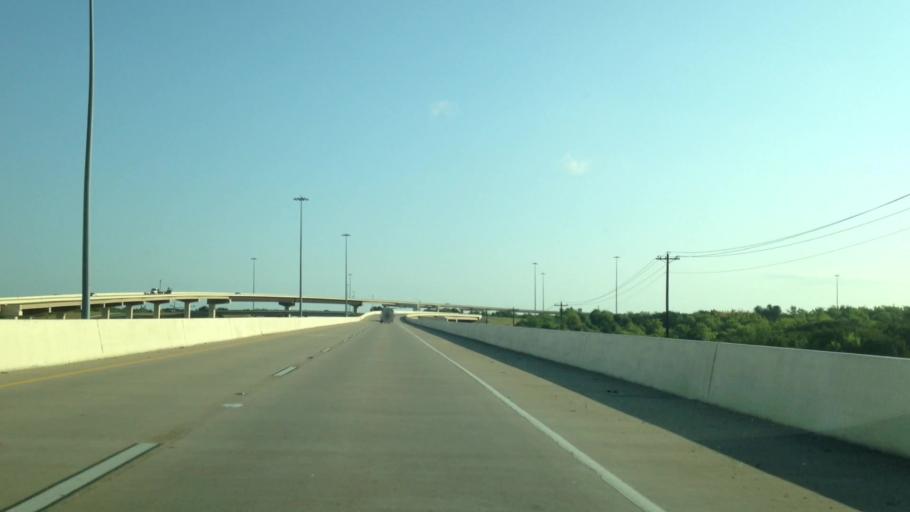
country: US
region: Texas
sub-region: Hays County
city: Buda
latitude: 30.1062
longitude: -97.8093
